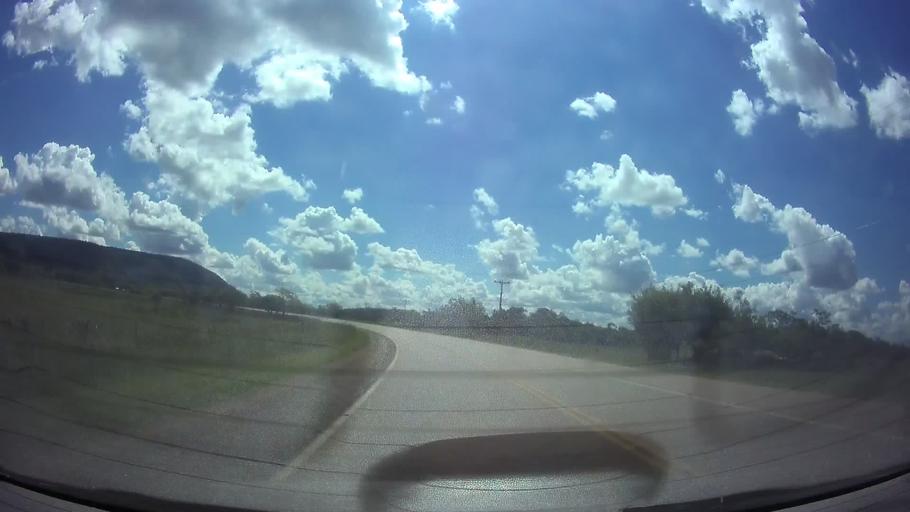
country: PY
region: Paraguari
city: La Colmena
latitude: -25.9138
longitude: -56.7114
